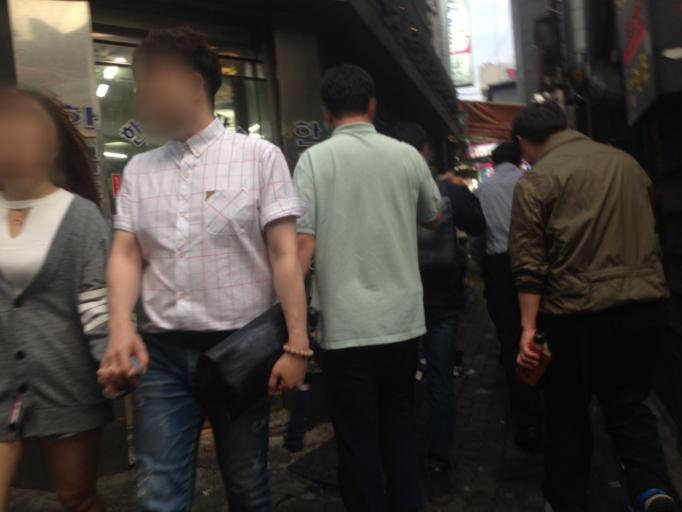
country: KR
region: Seoul
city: Seoul
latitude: 37.5701
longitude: 126.9914
